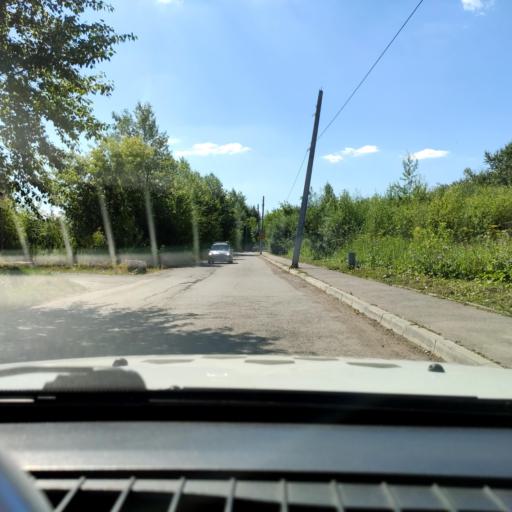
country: RU
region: Perm
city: Perm
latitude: 58.0275
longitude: 56.2230
